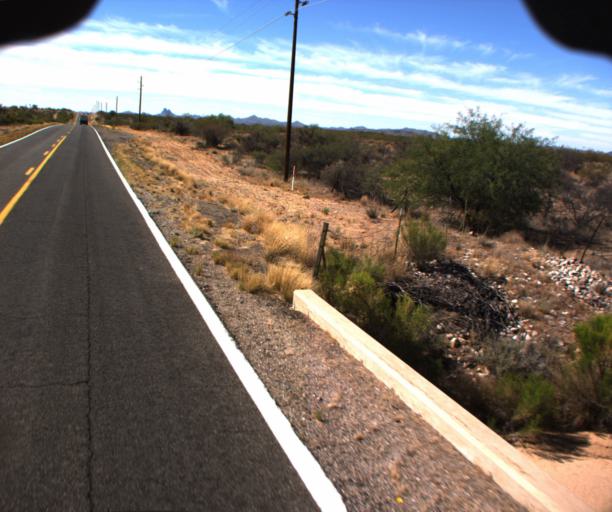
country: US
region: Arizona
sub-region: Yavapai County
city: Congress
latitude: 34.0689
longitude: -112.8210
